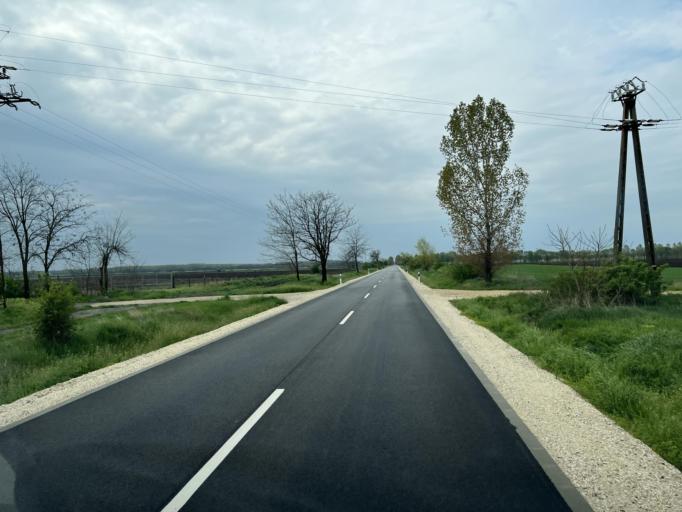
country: HU
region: Pest
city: Nyaregyhaza
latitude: 47.2455
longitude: 19.5209
